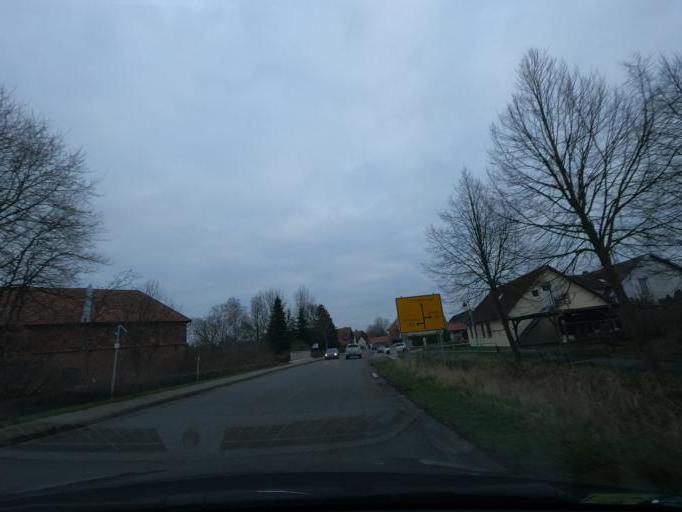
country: DE
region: Lower Saxony
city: Semmenstedt
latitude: 52.0954
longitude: 10.6951
